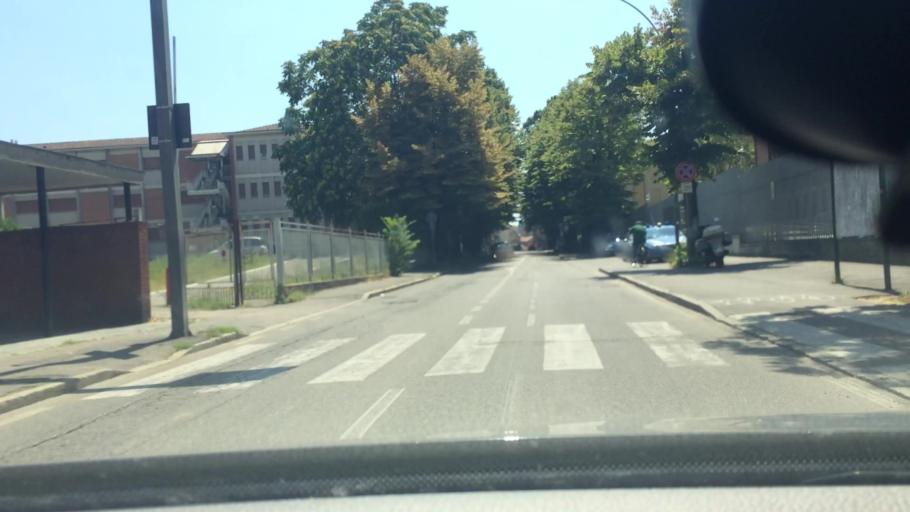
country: IT
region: Emilia-Romagna
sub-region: Provincia di Piacenza
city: Piacenza
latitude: 45.0515
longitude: 9.6849
